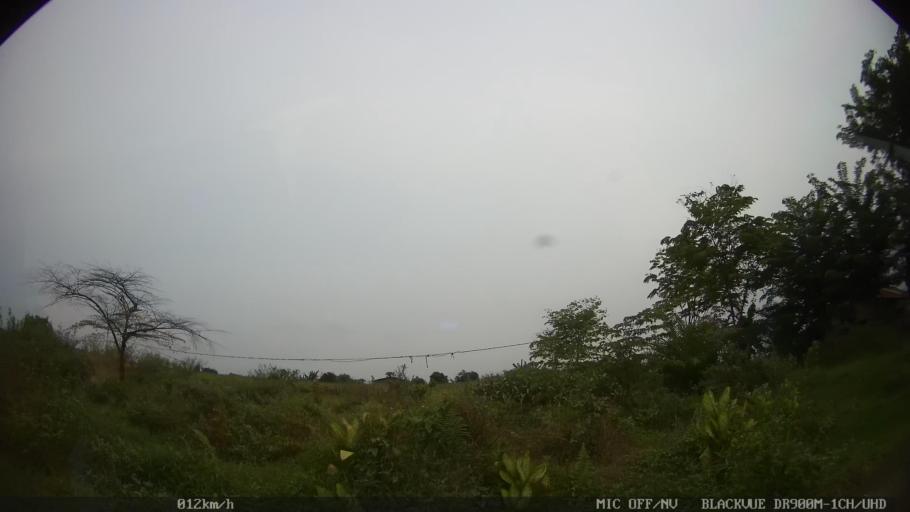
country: ID
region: North Sumatra
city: Medan
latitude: 3.5729
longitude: 98.7443
